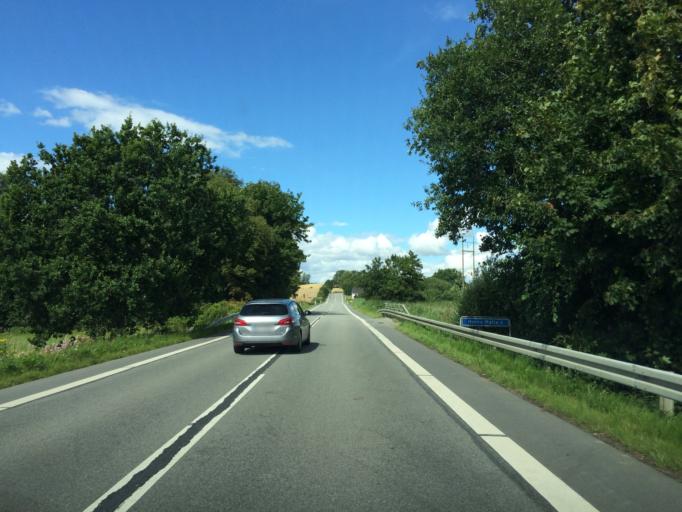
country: DK
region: South Denmark
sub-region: Faaborg-Midtfyn Kommune
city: Faaborg
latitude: 55.1194
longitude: 10.2140
